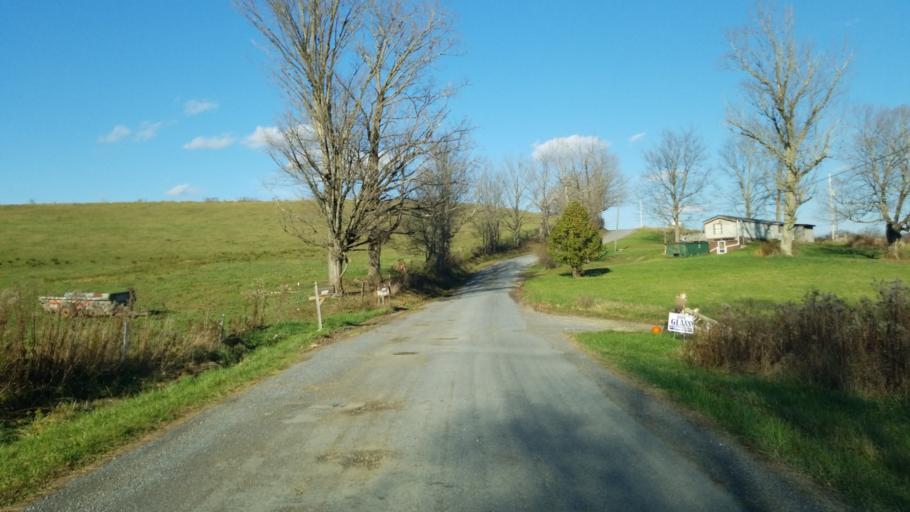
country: US
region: Pennsylvania
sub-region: Clearfield County
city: Treasure Lake
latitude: 41.1579
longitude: -78.6591
